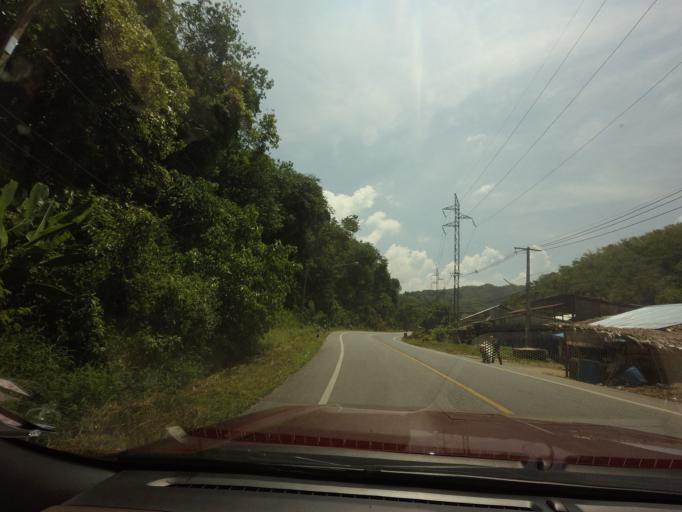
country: TH
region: Yala
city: Betong
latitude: 5.8269
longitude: 101.1123
